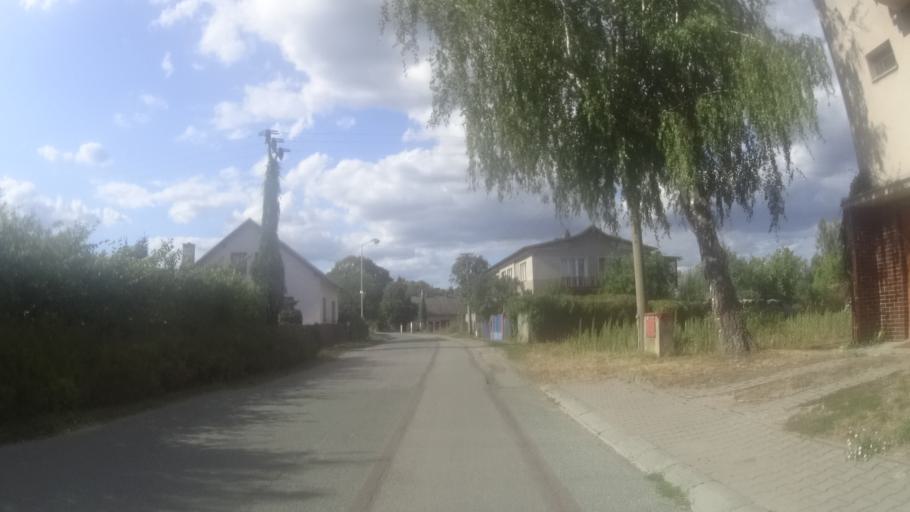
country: CZ
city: Albrechtice nad Orlici
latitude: 50.1465
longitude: 16.0609
